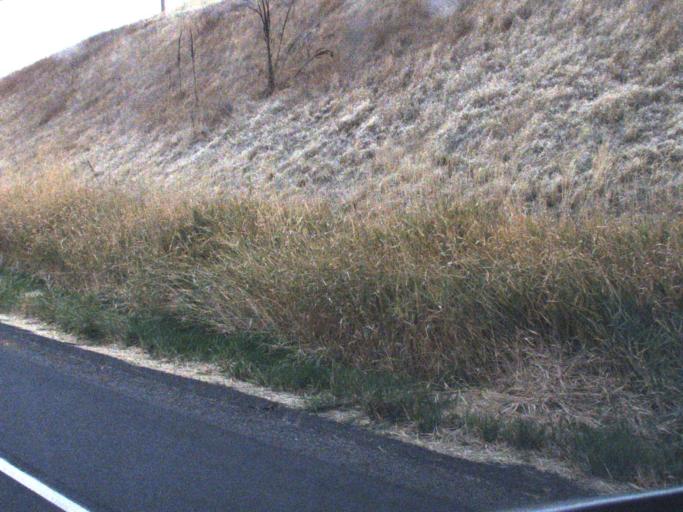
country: US
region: Washington
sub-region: Whitman County
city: Colfax
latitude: 46.9372
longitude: -117.3335
